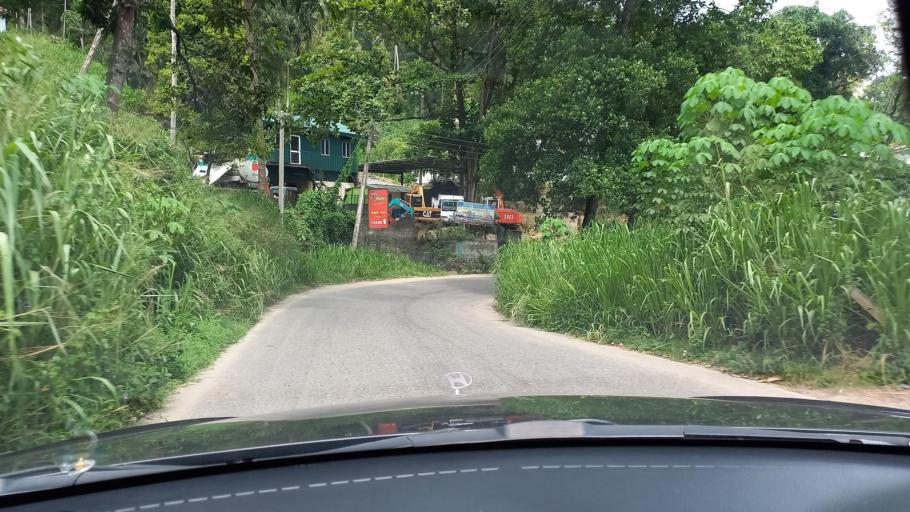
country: LK
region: Central
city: Kandy
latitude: 7.2453
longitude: 80.5987
